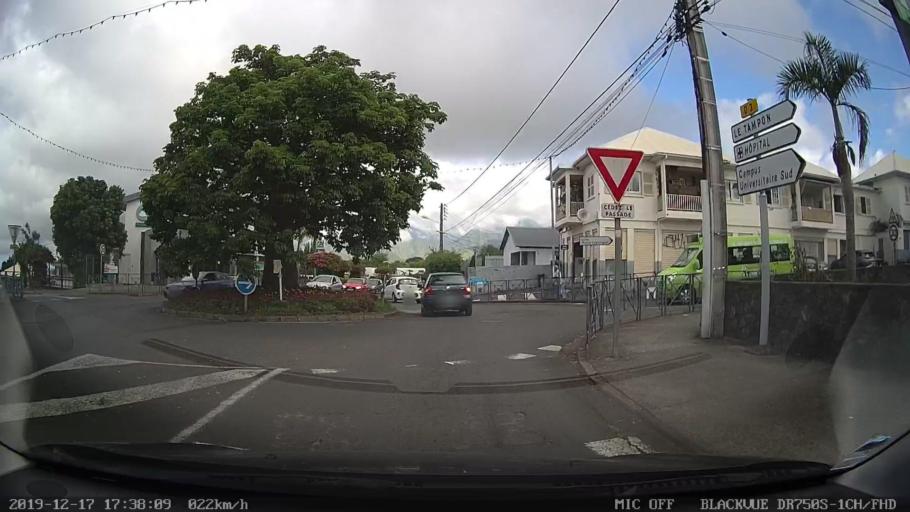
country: RE
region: Reunion
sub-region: Reunion
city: Le Tampon
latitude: -21.2605
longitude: 55.5037
